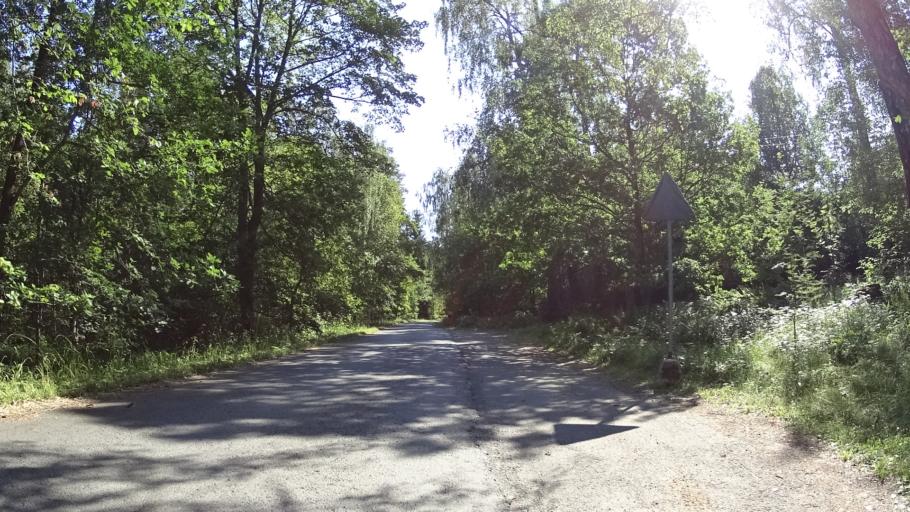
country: FI
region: Haeme
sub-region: Haemeenlinna
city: Haemeenlinna
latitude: 61.0263
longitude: 24.4490
